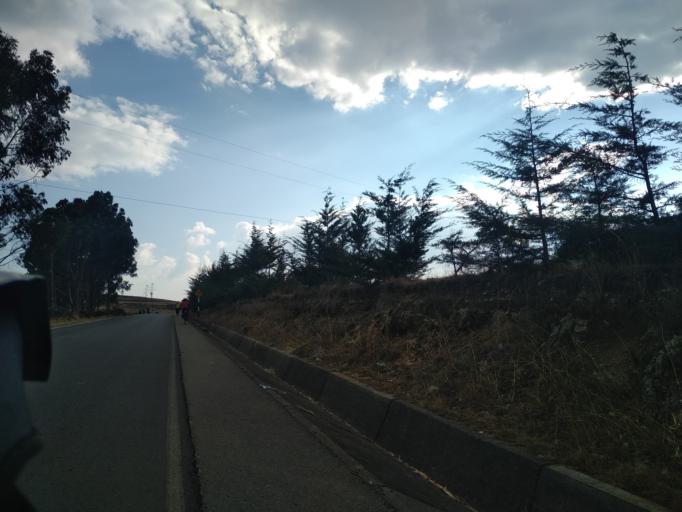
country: PE
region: Cajamarca
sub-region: Provincia de Cajamarca
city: Llacanora
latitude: -7.1455
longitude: -78.3950
